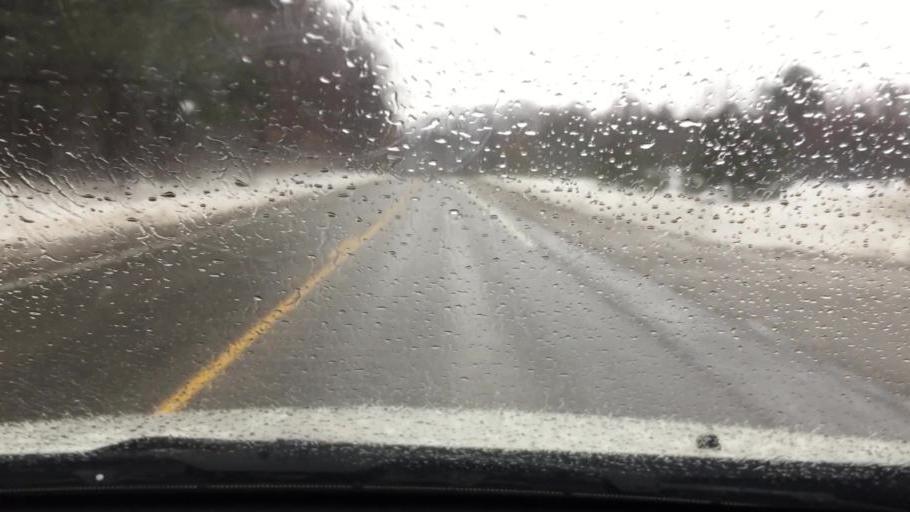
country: US
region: Michigan
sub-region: Charlevoix County
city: East Jordan
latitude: 45.2026
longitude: -85.1651
